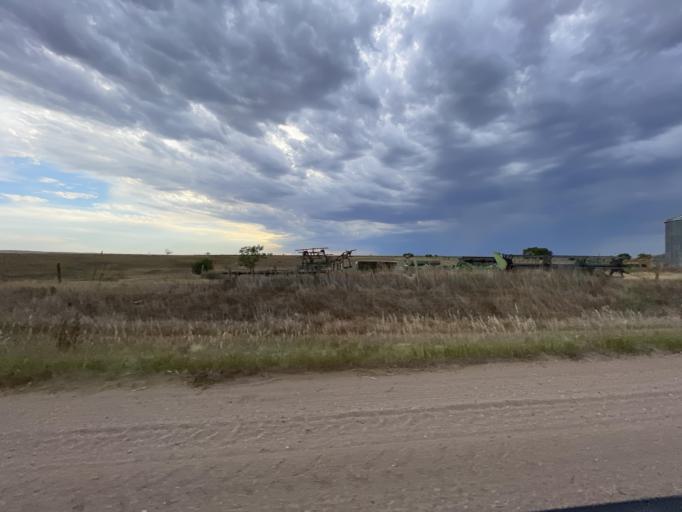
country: US
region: Nebraska
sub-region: Red Willow County
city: McCook
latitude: 40.2463
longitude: -100.7602
